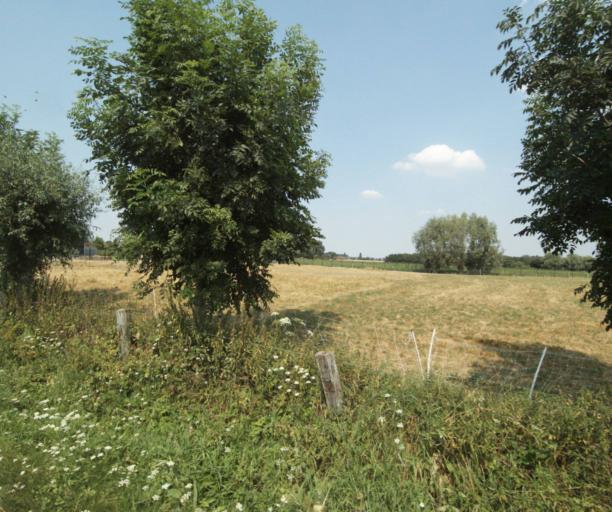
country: FR
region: Nord-Pas-de-Calais
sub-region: Departement du Nord
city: Quesnoy-sur-Deule
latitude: 50.7276
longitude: 3.0341
